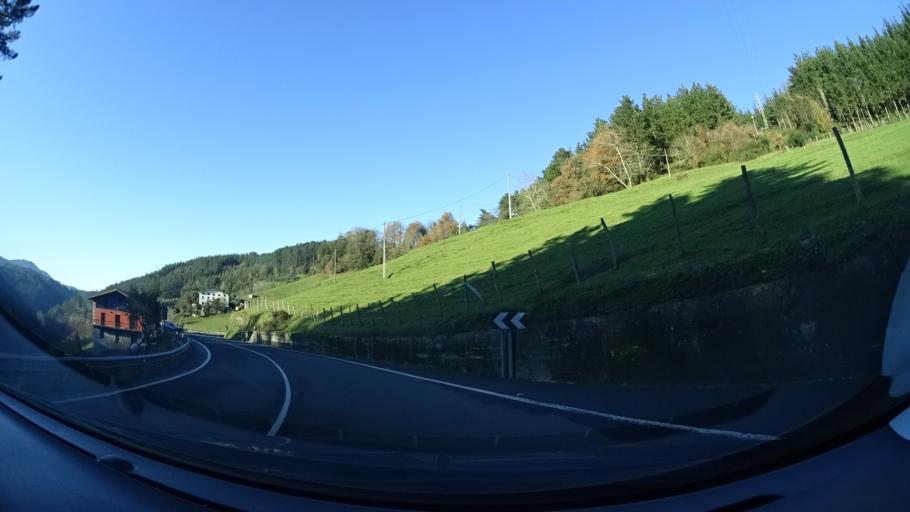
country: ES
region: Basque Country
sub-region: Bizkaia
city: Berriatua
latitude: 43.3159
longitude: -2.4776
